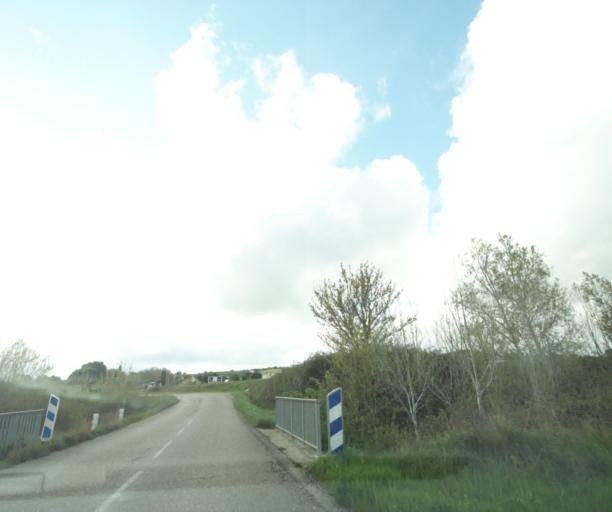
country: FR
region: Languedoc-Roussillon
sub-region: Departement de l'Herault
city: Laverune
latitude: 43.5856
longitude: 3.7915
